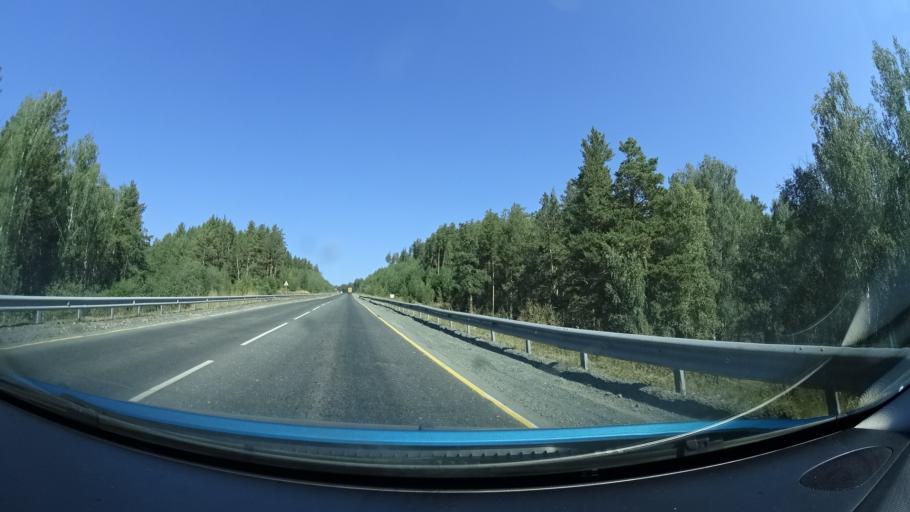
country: RU
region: Bashkortostan
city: Abzakovo
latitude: 53.8817
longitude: 58.5306
